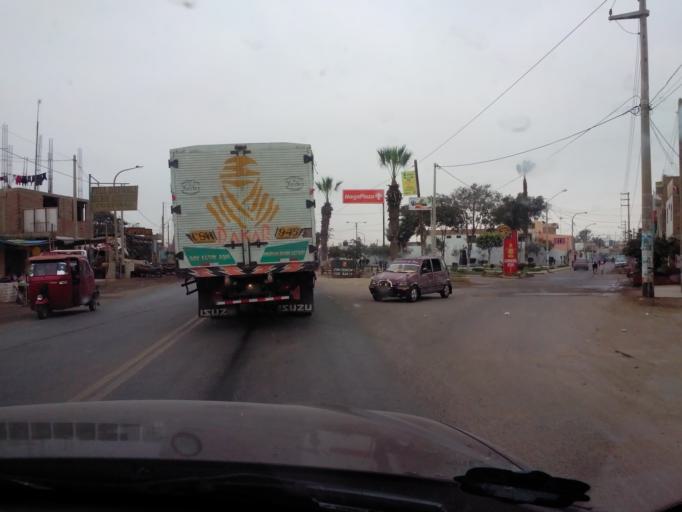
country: PE
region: Ica
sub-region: Provincia de Chincha
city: Chincha Alta
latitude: -13.4262
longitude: -76.1340
